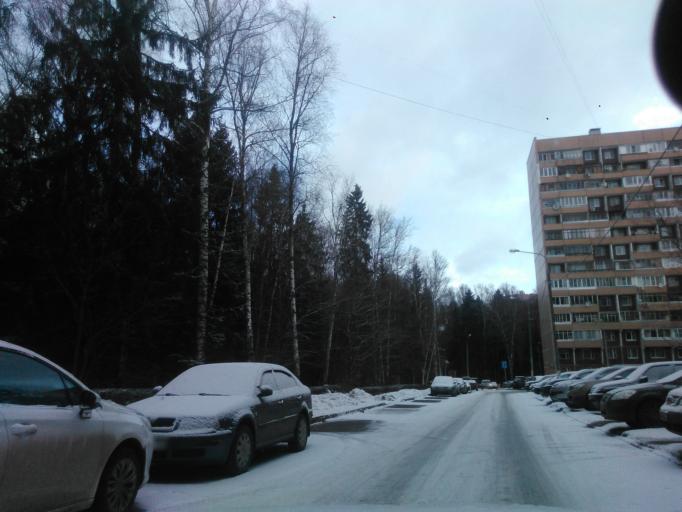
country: RU
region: Moscow
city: Zelenograd
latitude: 55.9955
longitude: 37.1740
